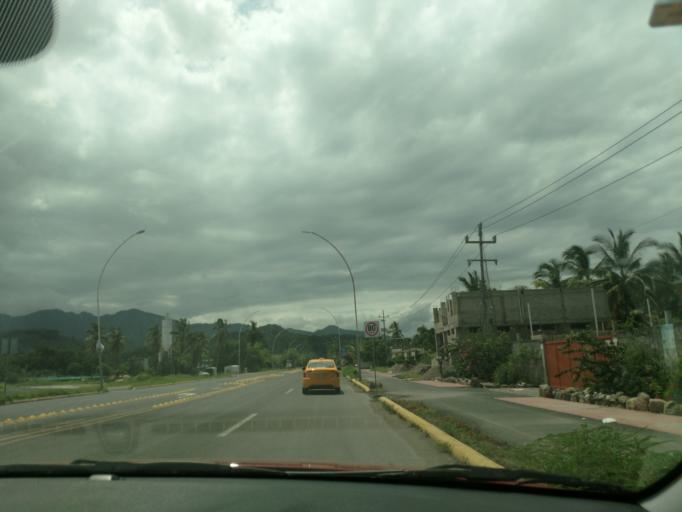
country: MX
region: Nayarit
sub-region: San Blas
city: Aticama
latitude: 21.5013
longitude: -105.2037
